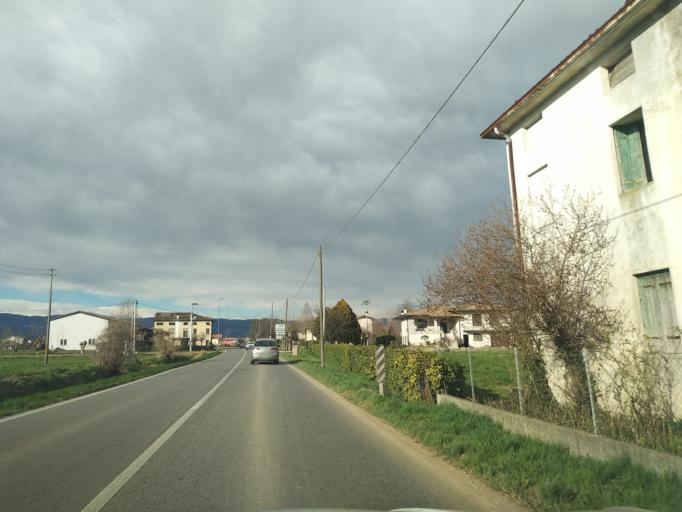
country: IT
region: Veneto
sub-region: Provincia di Vicenza
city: Poianella
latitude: 45.6245
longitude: 11.6226
